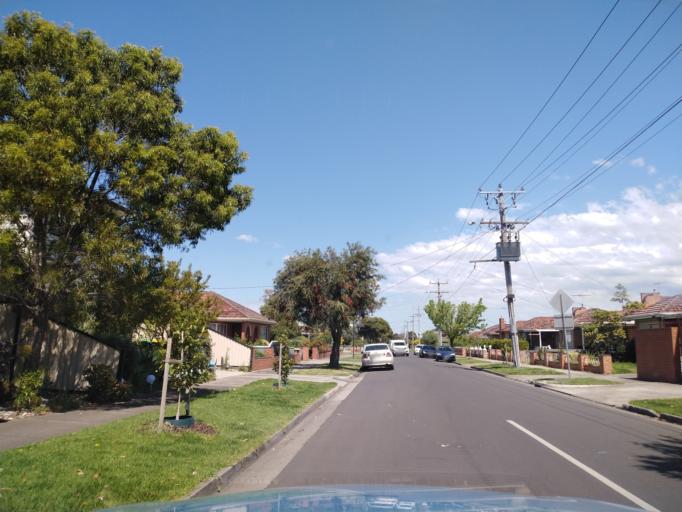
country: AU
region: Victoria
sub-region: Hobsons Bay
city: Altona North
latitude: -37.8325
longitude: 144.8584
